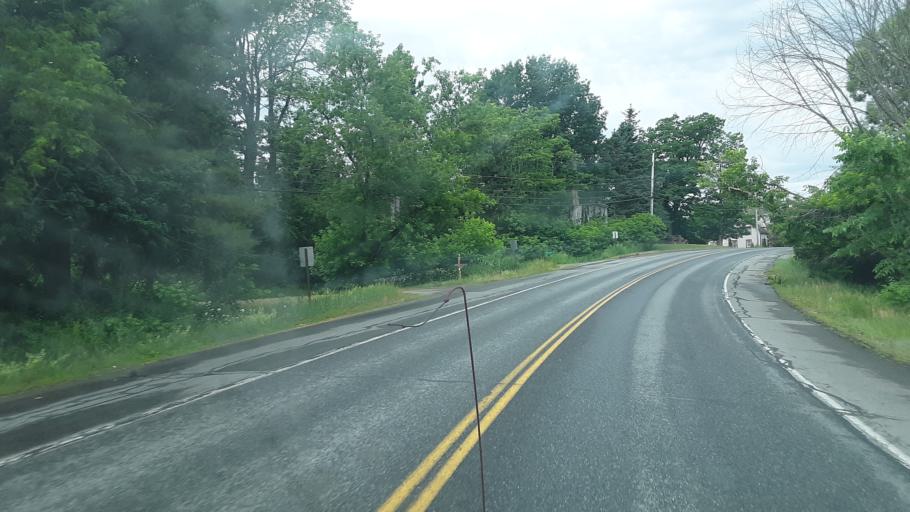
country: US
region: Maine
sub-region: Penobscot County
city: Eddington
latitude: 44.8178
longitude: -68.7083
